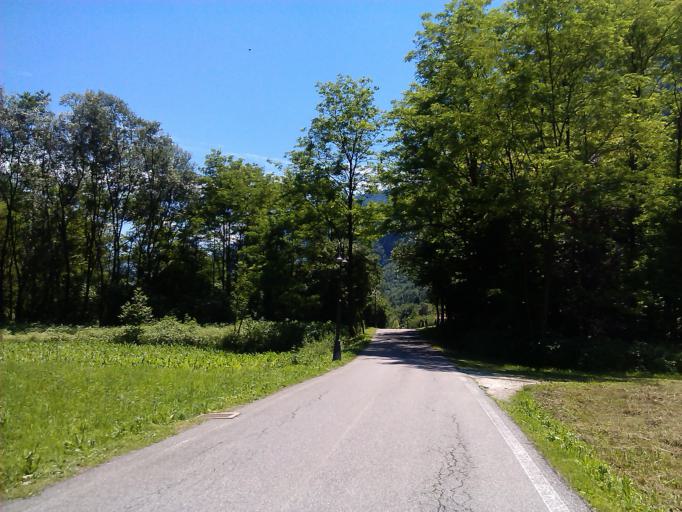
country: IT
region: Trentino-Alto Adige
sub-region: Provincia di Trento
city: Grigno
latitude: 45.9881
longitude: 11.6670
